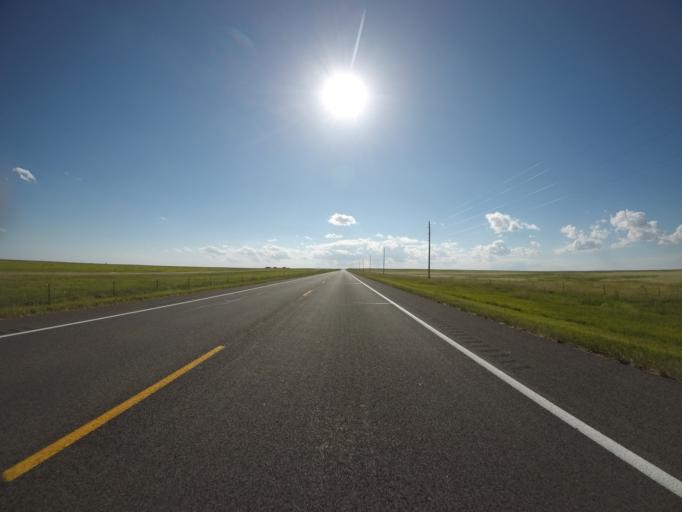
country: US
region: Colorado
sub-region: Morgan County
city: Brush
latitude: 40.6097
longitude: -103.6979
